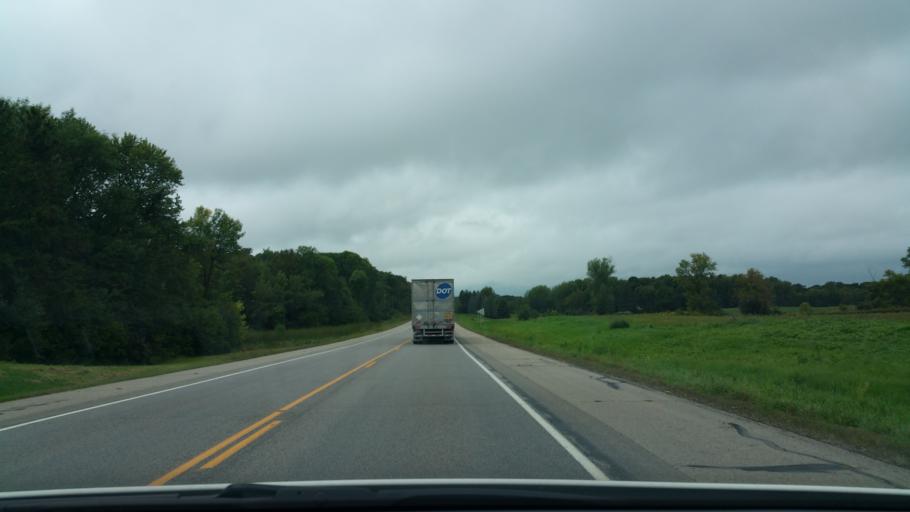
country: US
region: Minnesota
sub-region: Rice County
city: Dundas
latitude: 44.4718
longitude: -93.2744
